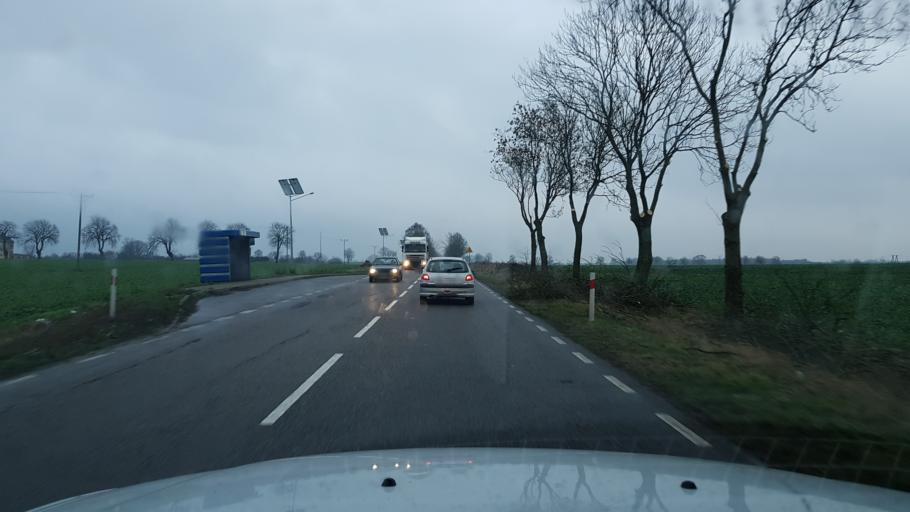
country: PL
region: West Pomeranian Voivodeship
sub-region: Powiat gryficki
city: Ploty
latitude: 53.8470
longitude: 15.2318
